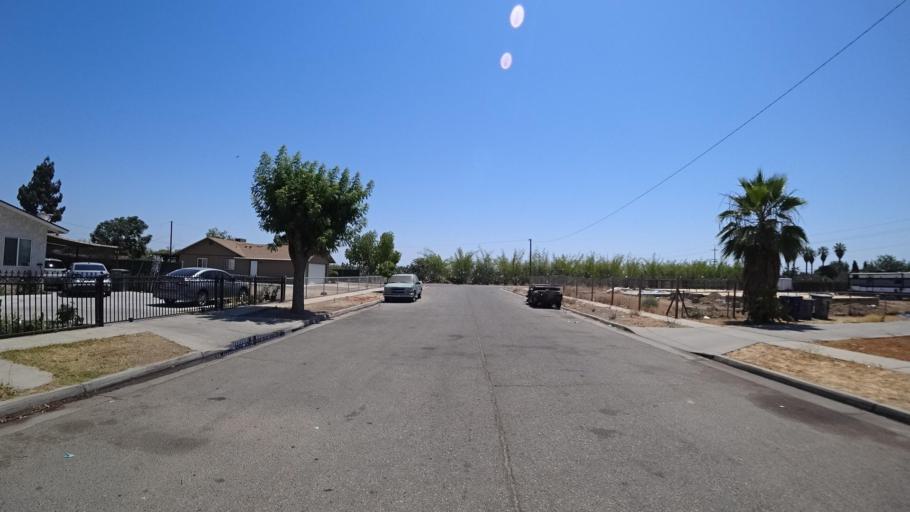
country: US
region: California
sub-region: Fresno County
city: West Park
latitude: 36.7078
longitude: -119.8073
